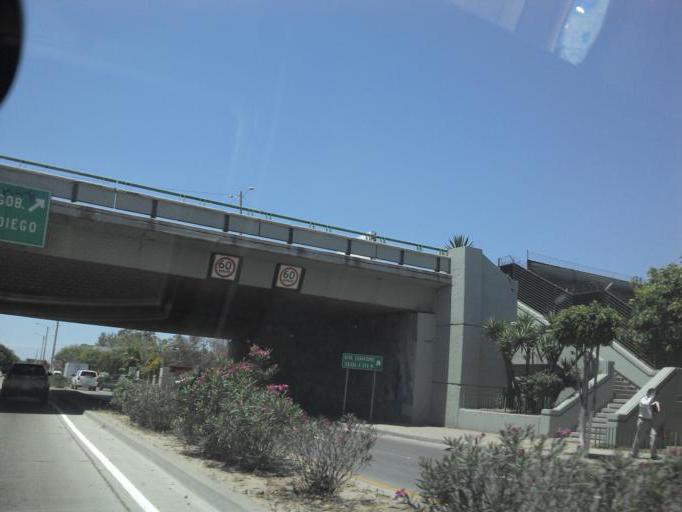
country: MX
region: Baja California
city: Tijuana
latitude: 32.5277
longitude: -117.0144
